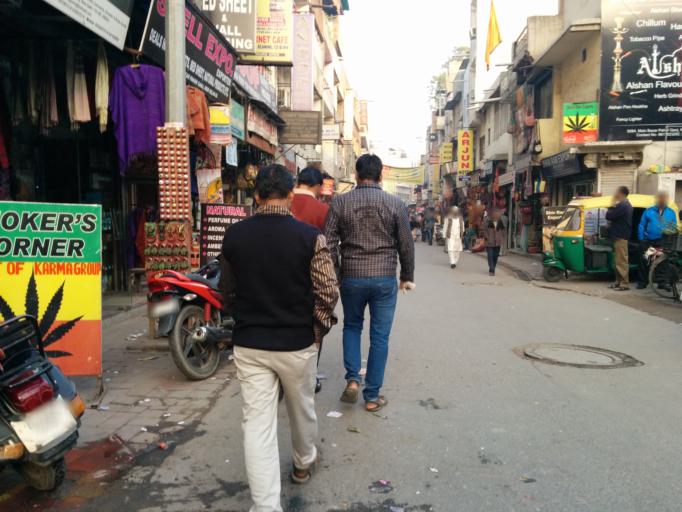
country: IN
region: NCT
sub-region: New Delhi
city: New Delhi
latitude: 28.6408
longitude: 77.2117
